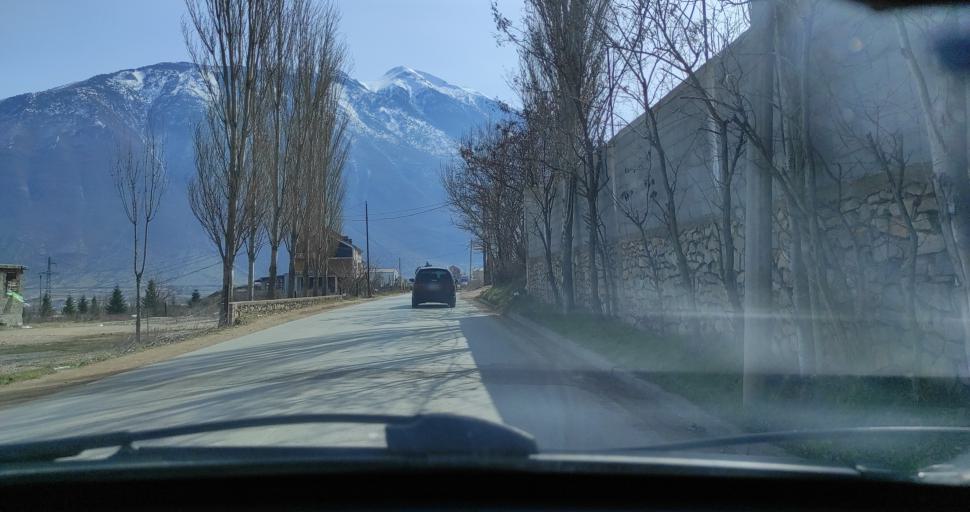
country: AL
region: Kukes
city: Kukes
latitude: 42.0709
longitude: 20.4300
